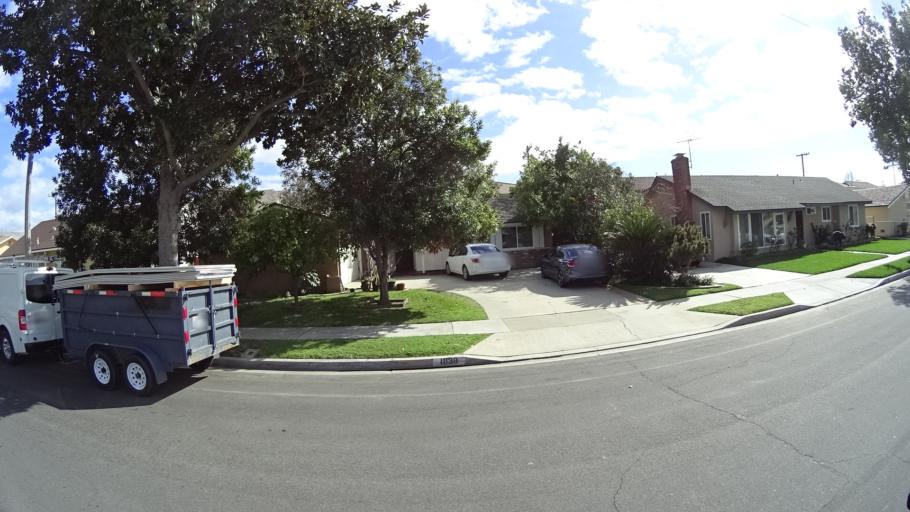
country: US
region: California
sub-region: Orange County
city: Anaheim
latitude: 33.8268
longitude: -117.9475
